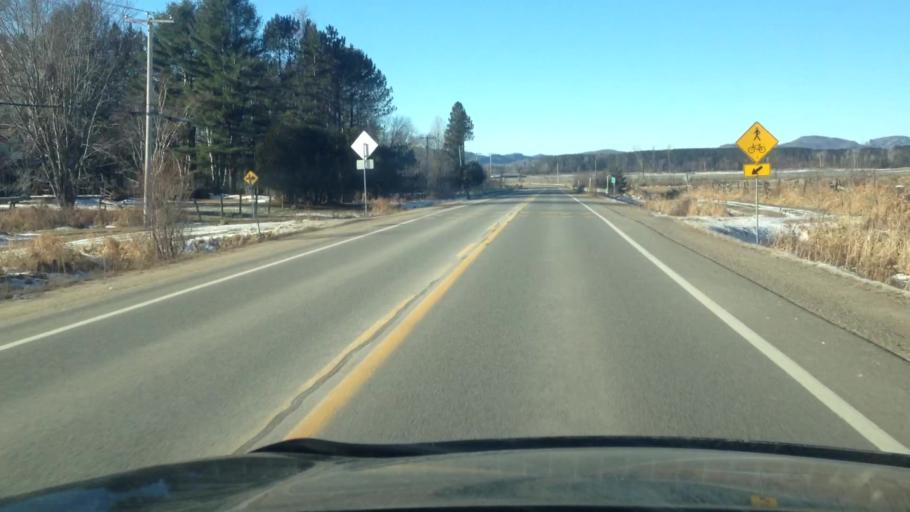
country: CA
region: Quebec
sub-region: Laurentides
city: Mont-Tremblant
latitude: 45.9610
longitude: -74.5814
